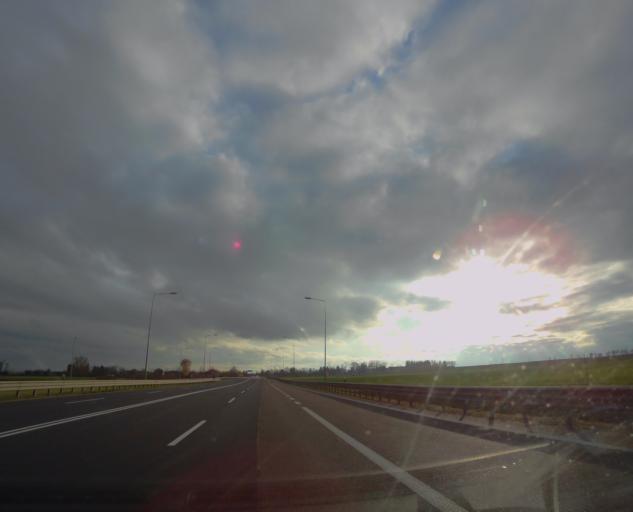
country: PL
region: Subcarpathian Voivodeship
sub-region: Powiat przemyski
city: Orly
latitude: 49.9068
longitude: 22.8179
